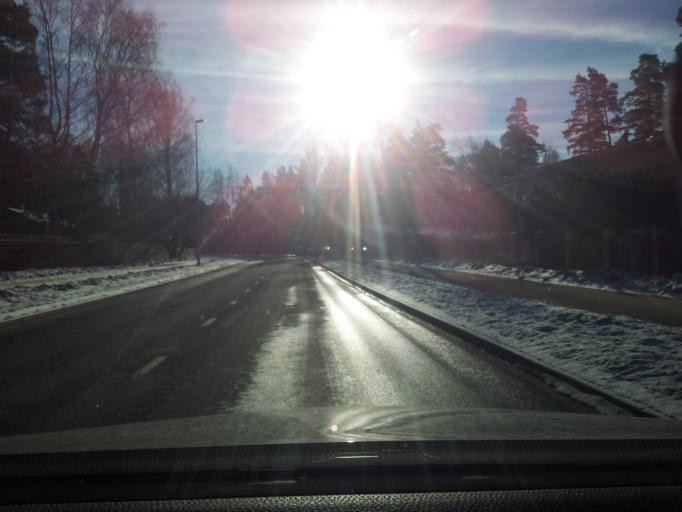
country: FI
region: Uusimaa
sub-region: Helsinki
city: Koukkuniemi
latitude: 60.1494
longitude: 24.7381
